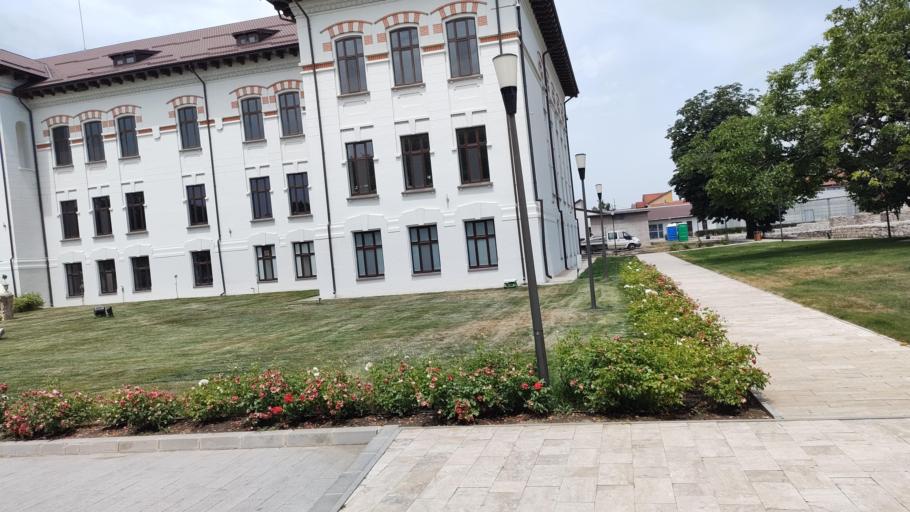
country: RO
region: Mehedinti
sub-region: Municipiul Drobeta-Turnu Severin
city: Drobeta-Turnu Severin
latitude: 44.6246
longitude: 22.6670
